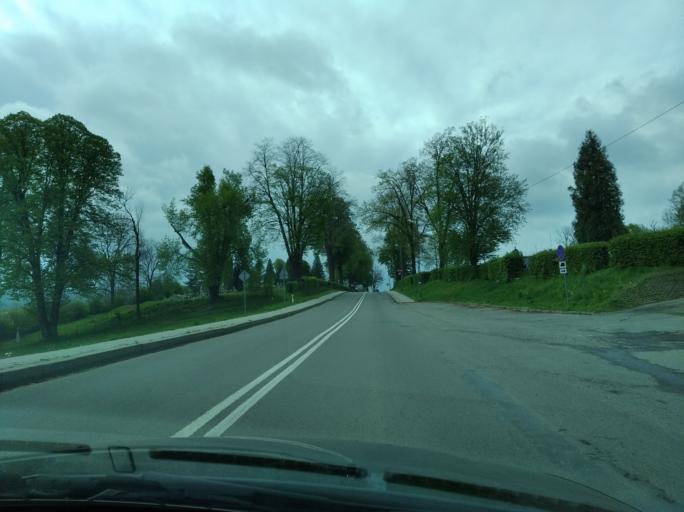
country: PL
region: Subcarpathian Voivodeship
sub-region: Powiat rzeszowski
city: Dynow
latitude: 49.8225
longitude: 22.2344
